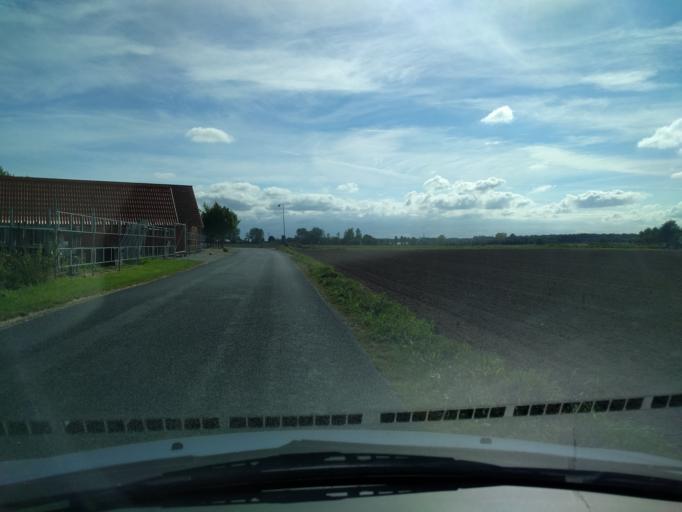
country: DK
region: South Denmark
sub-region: Kerteminde Kommune
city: Munkebo
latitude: 55.4138
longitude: 10.5763
